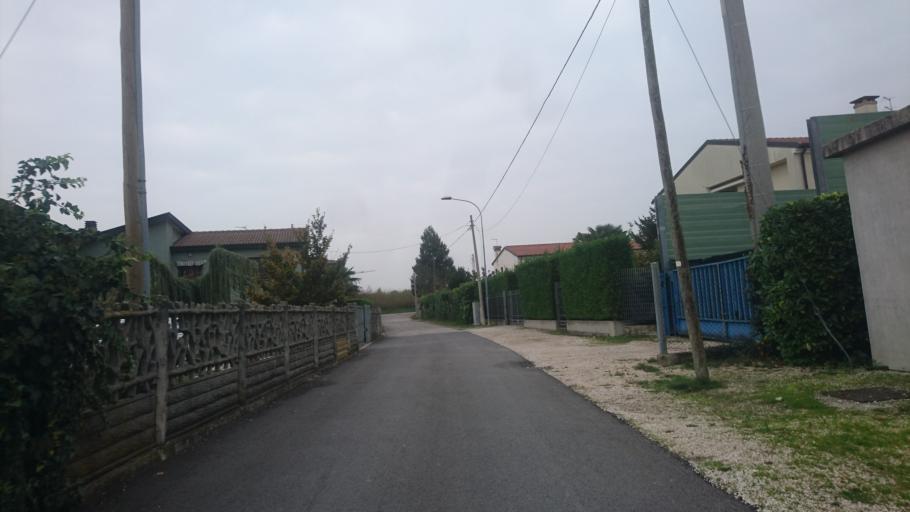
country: IT
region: Veneto
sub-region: Provincia di Padova
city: Oltre Brenta
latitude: 45.4069
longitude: 11.9920
